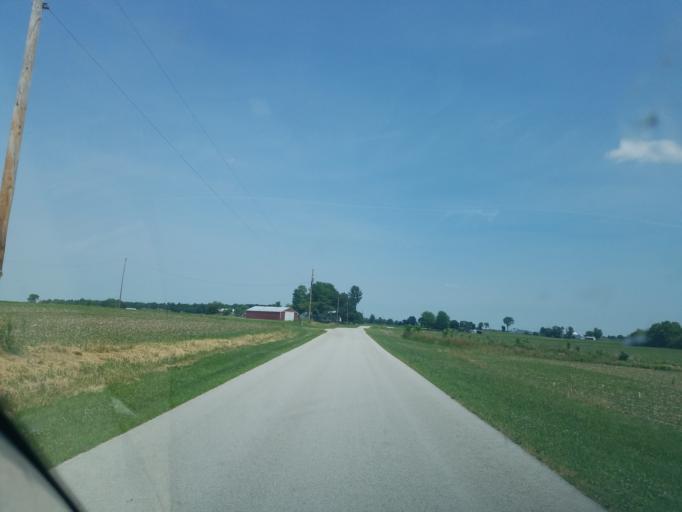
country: US
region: Ohio
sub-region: Wyandot County
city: Carey
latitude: 40.9516
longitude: -83.4915
